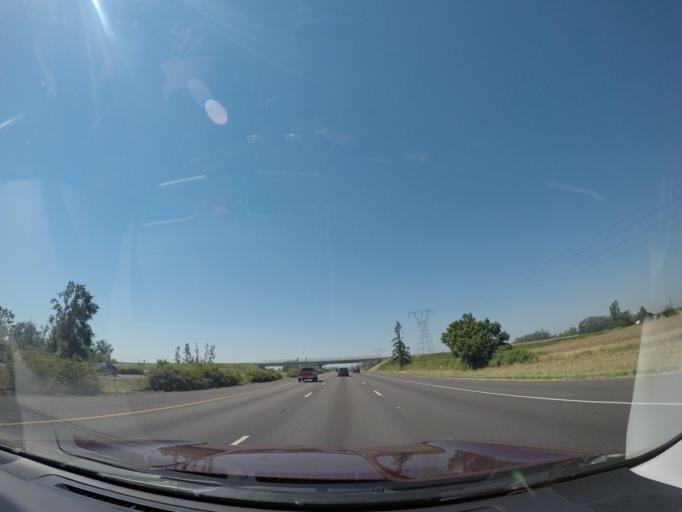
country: US
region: Oregon
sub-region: Marion County
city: Gervais
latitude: 45.1168
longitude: -122.9160
